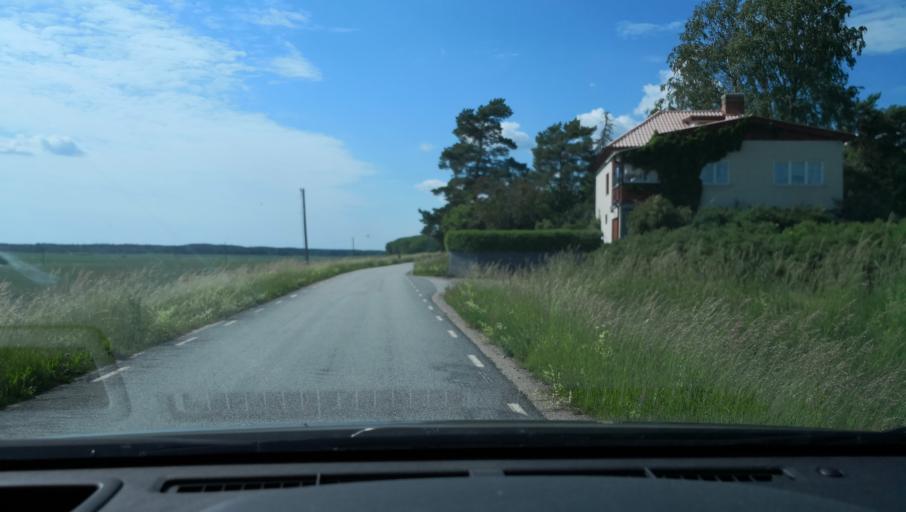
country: SE
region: Uppsala
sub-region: Enkopings Kommun
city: Orsundsbro
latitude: 59.8178
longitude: 17.3334
